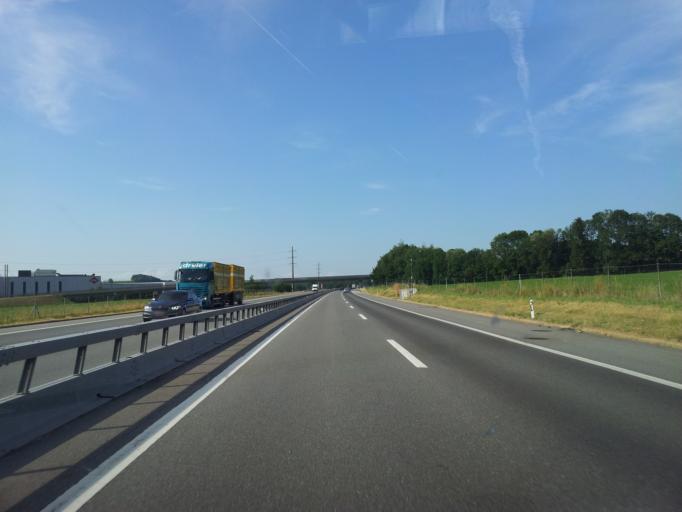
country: CH
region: Fribourg
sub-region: Veveyse District
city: Chatel-Saint-Denis
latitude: 46.5653
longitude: 6.9173
